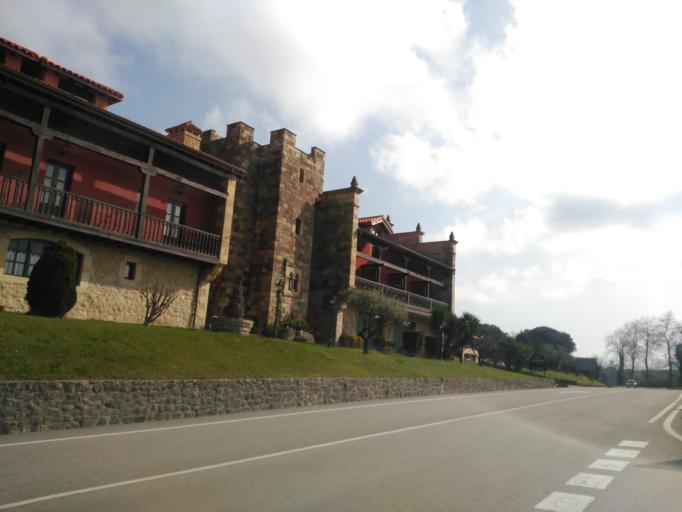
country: ES
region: Cantabria
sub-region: Provincia de Cantabria
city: Santillana
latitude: 43.3852
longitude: -4.1082
